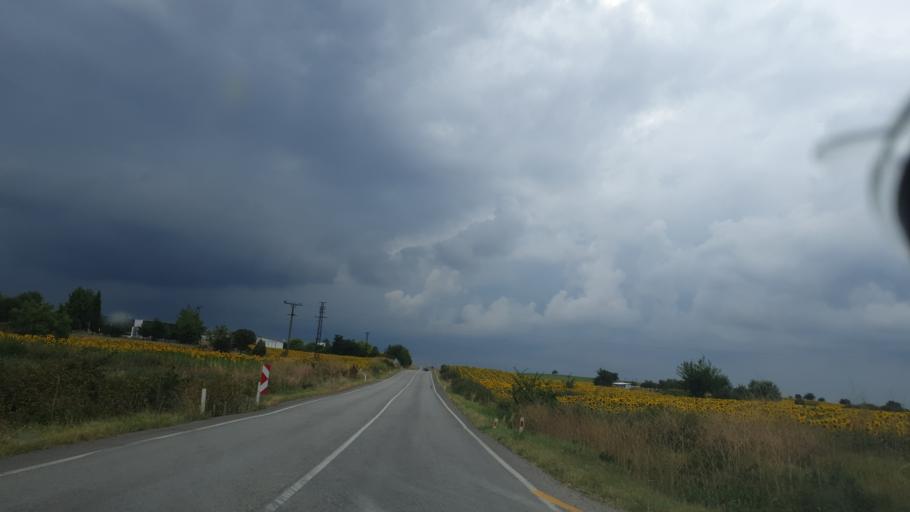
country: TR
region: Tekirdag
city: Hayrabolu
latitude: 41.2194
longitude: 27.0751
